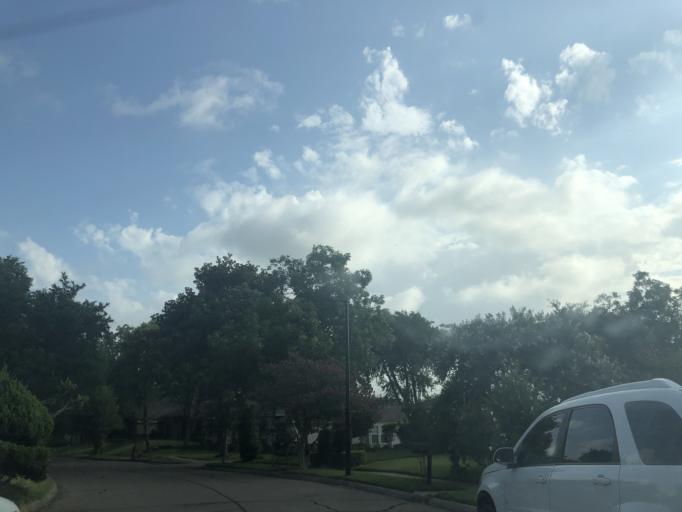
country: US
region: Texas
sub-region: Dallas County
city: Garland
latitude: 32.8598
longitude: -96.6261
